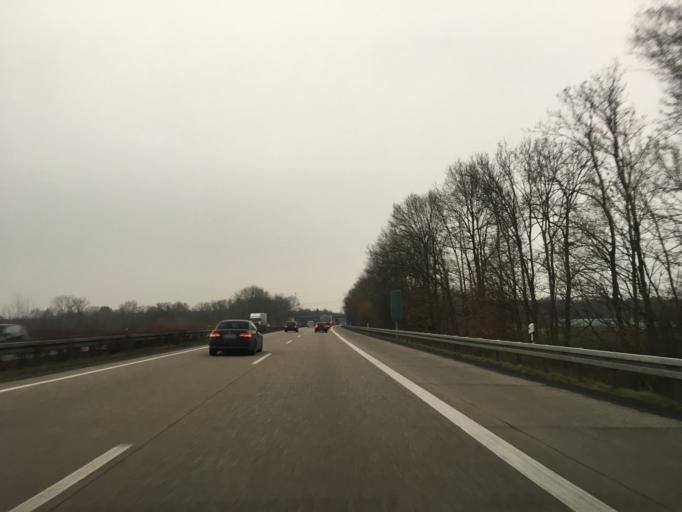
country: DE
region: North Rhine-Westphalia
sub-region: Regierungsbezirk Munster
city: Ascheberg
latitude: 51.8358
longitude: 7.5920
